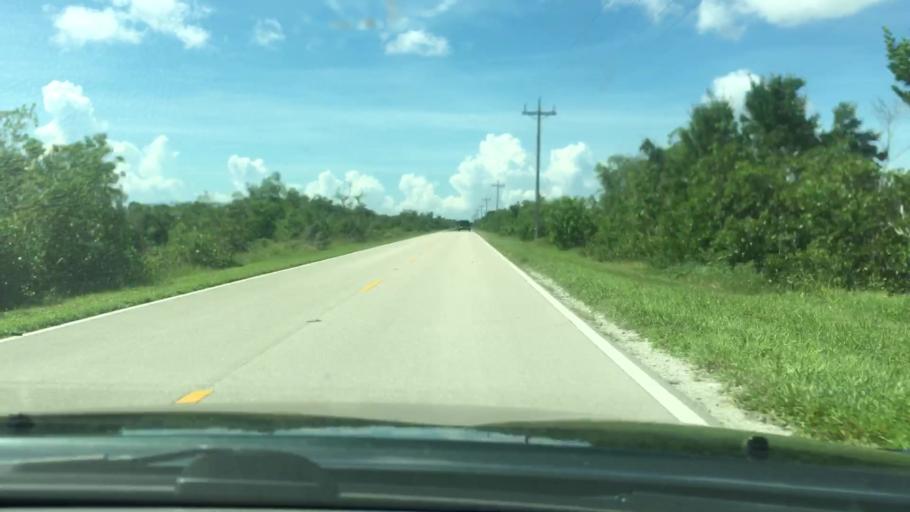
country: US
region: Florida
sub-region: Collier County
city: Marco
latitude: 25.9485
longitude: -81.6426
